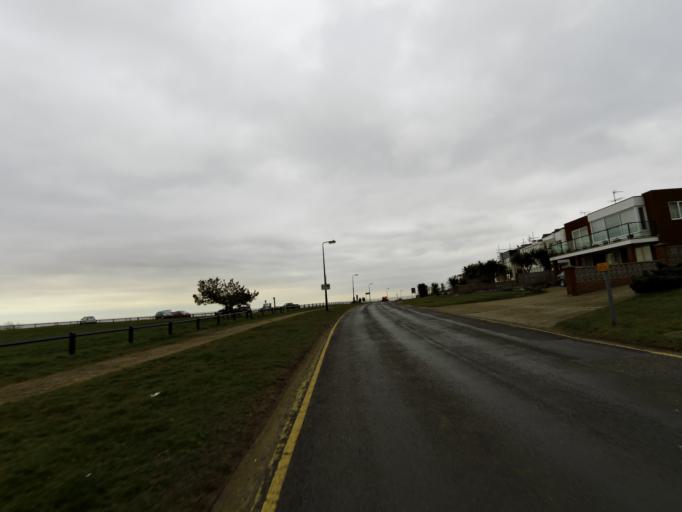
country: GB
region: England
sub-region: Suffolk
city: Felixstowe
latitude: 51.9760
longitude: 1.3802
